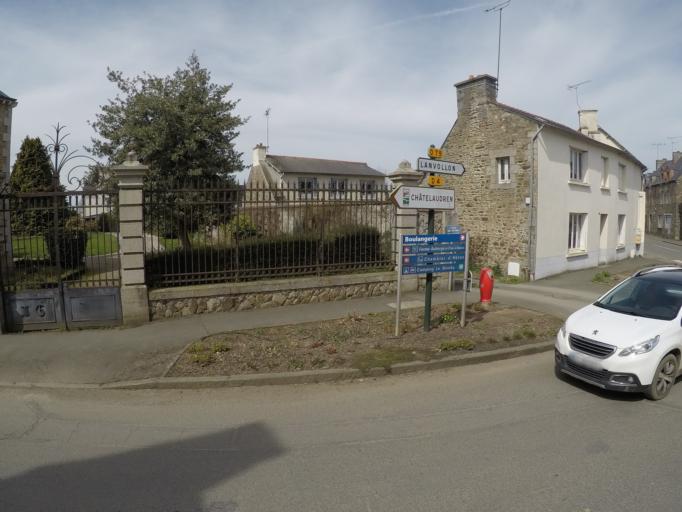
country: FR
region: Brittany
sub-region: Departement des Cotes-d'Armor
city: Plelo
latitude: 48.5567
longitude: -2.9465
